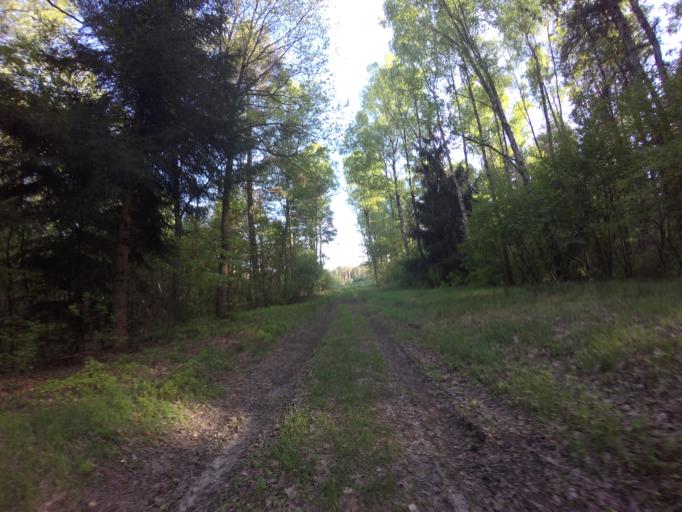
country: PL
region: West Pomeranian Voivodeship
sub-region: Powiat choszczenski
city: Drawno
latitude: 53.2262
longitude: 15.6844
